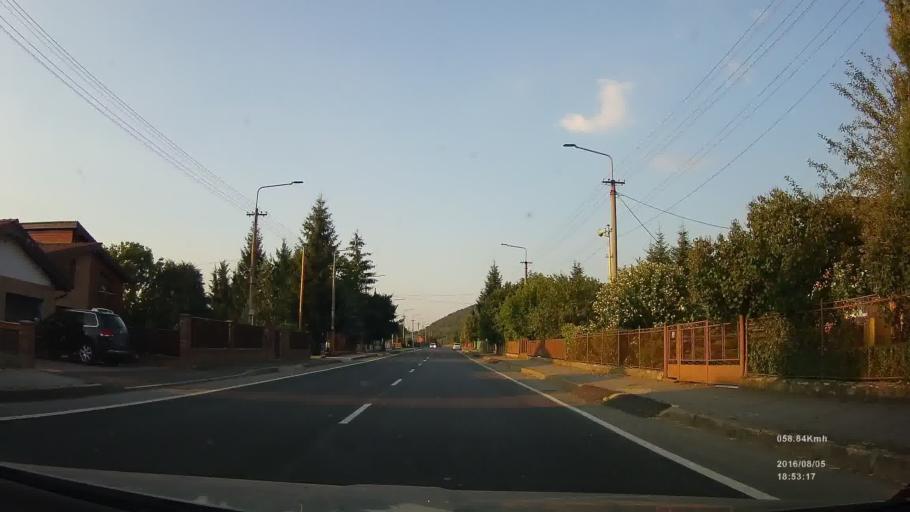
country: SK
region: Presovsky
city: Stropkov
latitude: 49.2150
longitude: 21.6579
